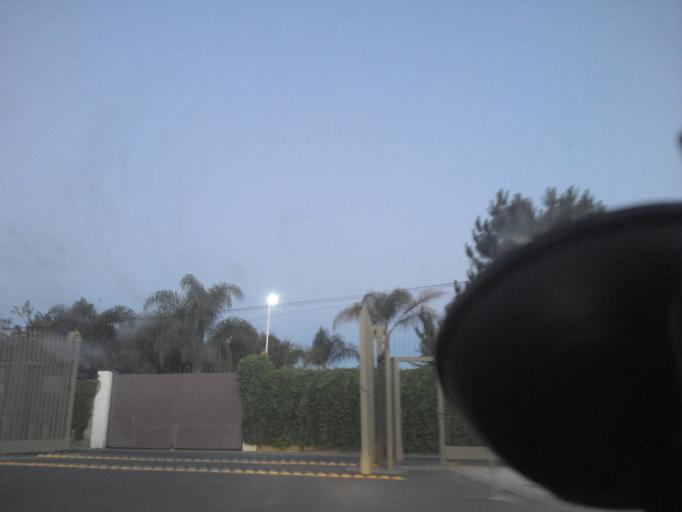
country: MX
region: Jalisco
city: Nuevo Mexico
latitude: 20.6996
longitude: -103.4703
